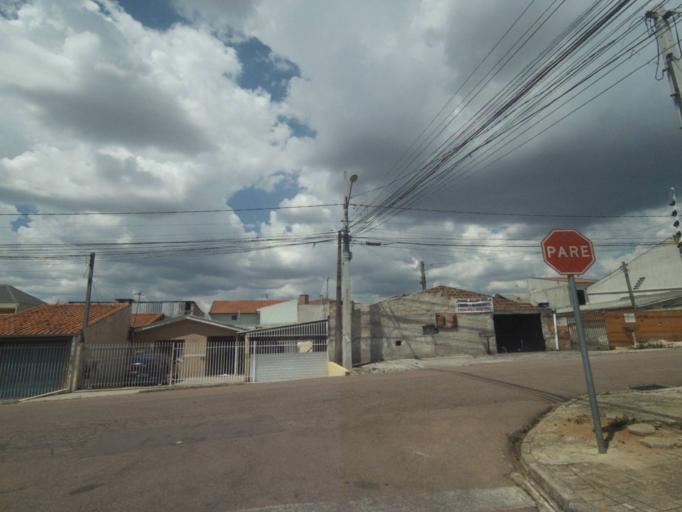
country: BR
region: Parana
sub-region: Sao Jose Dos Pinhais
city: Sao Jose dos Pinhais
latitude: -25.5356
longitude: -49.2778
